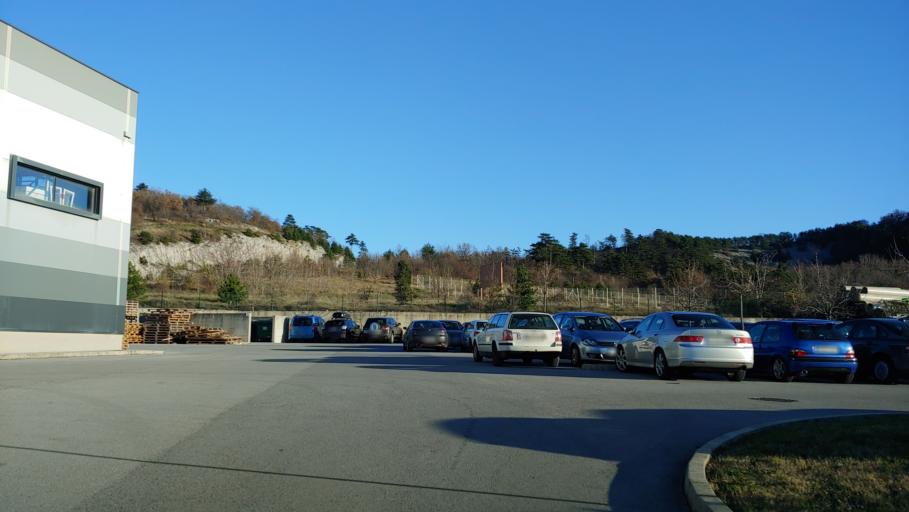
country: SI
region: Sezana
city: Sezana
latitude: 45.7102
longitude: 13.8563
